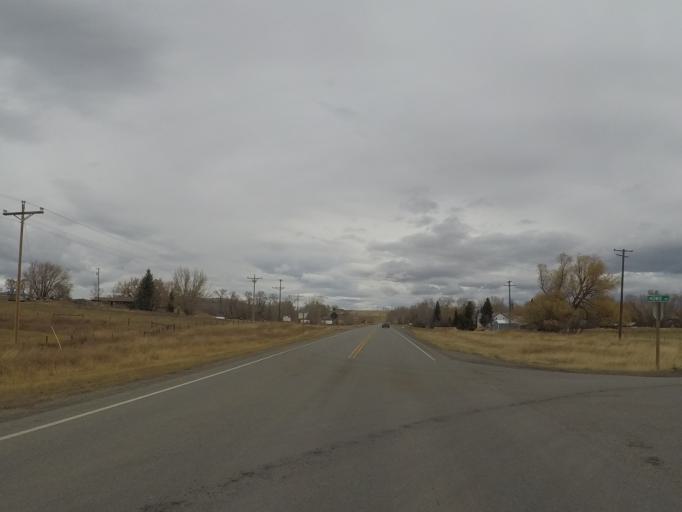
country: US
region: Montana
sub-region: Sweet Grass County
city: Big Timber
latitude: 45.8536
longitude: -109.9396
